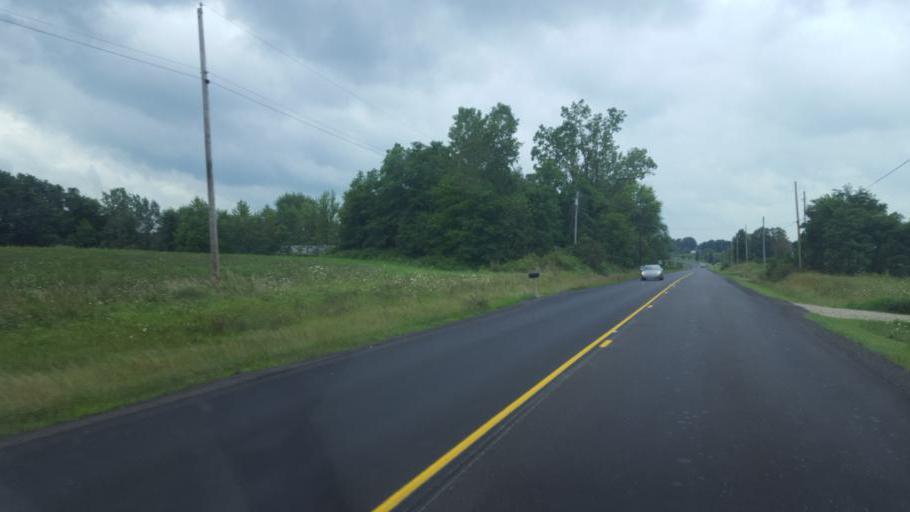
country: US
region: Ohio
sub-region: Morrow County
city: Mount Gilead
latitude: 40.5846
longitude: -82.7225
